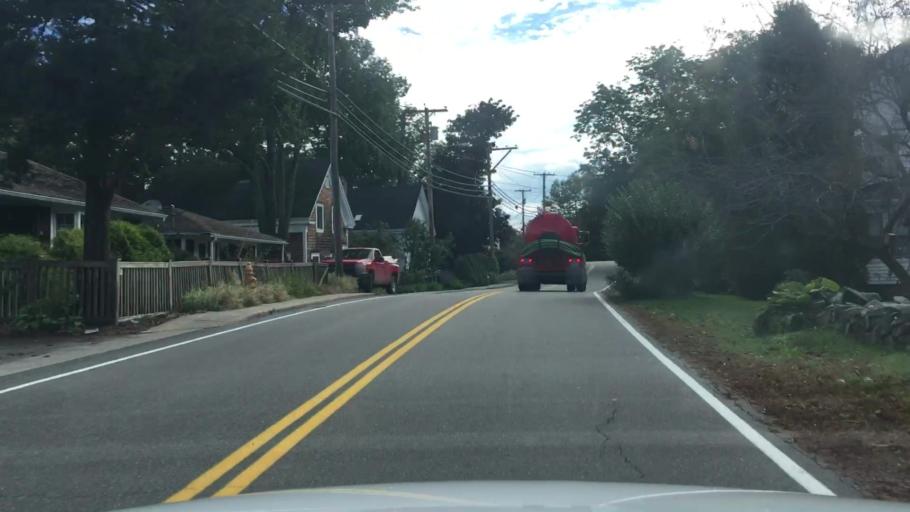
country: US
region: Maine
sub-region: York County
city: Kittery Point
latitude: 43.0833
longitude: -70.7017
